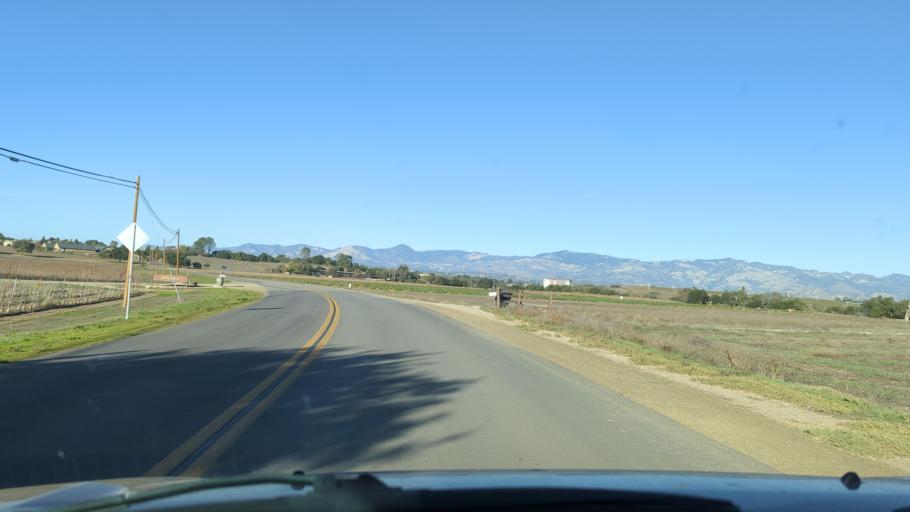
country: US
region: California
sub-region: Santa Barbara County
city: Santa Ynez
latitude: 34.5925
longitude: -120.0985
